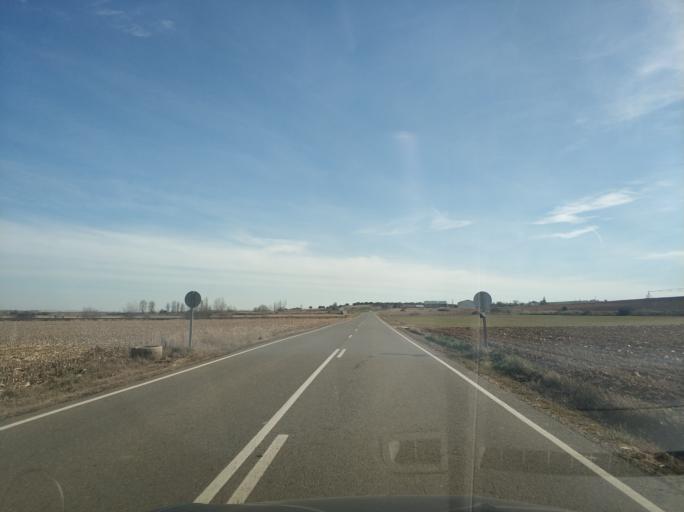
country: ES
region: Castille and Leon
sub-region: Provincia de Salamanca
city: Florida de Liebana
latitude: 41.0332
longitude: -5.7671
